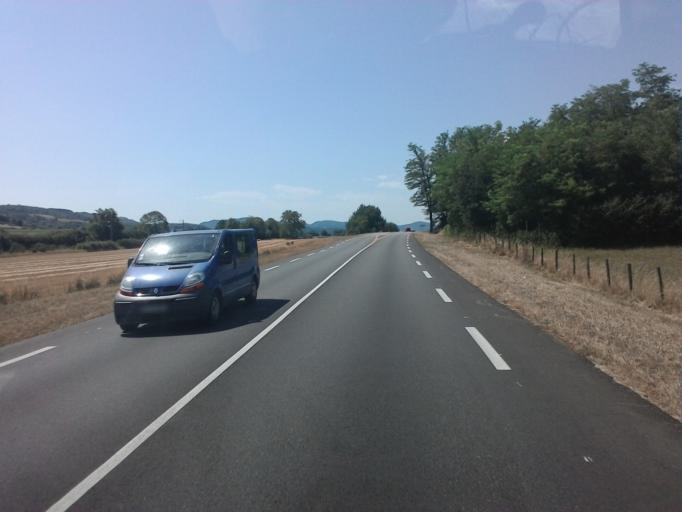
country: FR
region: Franche-Comte
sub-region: Departement du Jura
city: Montmorot
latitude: 46.6503
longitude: 5.5080
